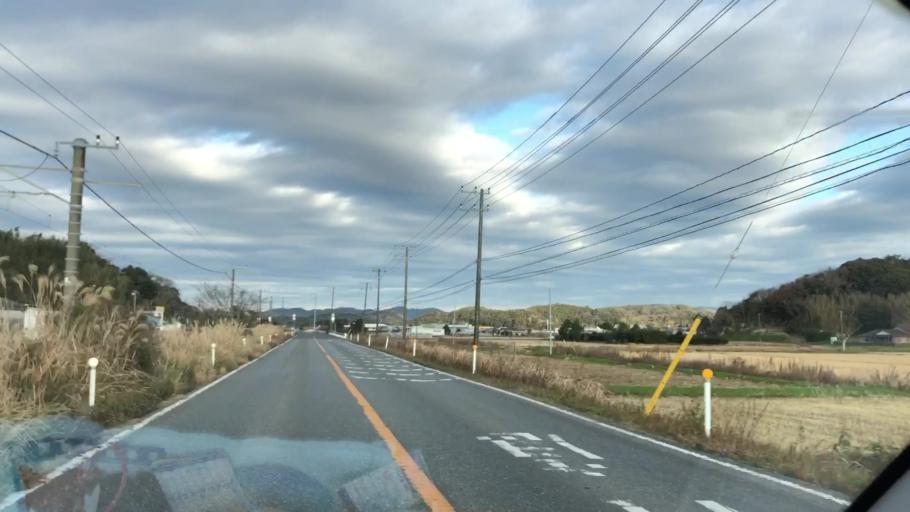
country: JP
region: Chiba
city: Tateyama
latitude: 34.9944
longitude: 139.9195
